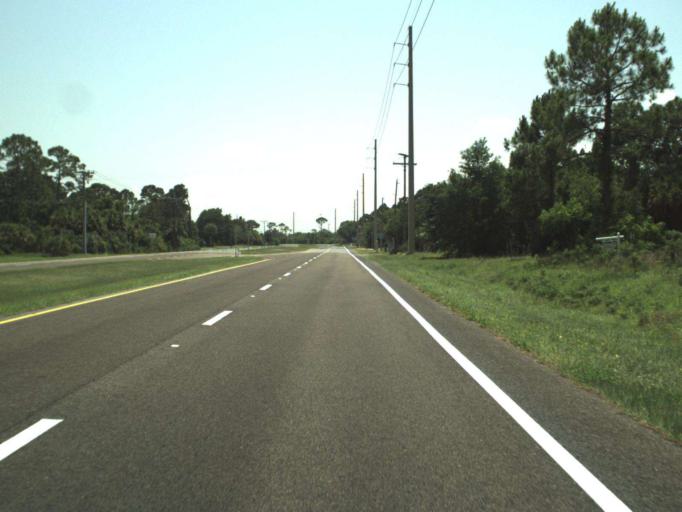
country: US
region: Florida
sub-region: Volusia County
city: Oak Hill
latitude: 28.7924
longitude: -80.8825
